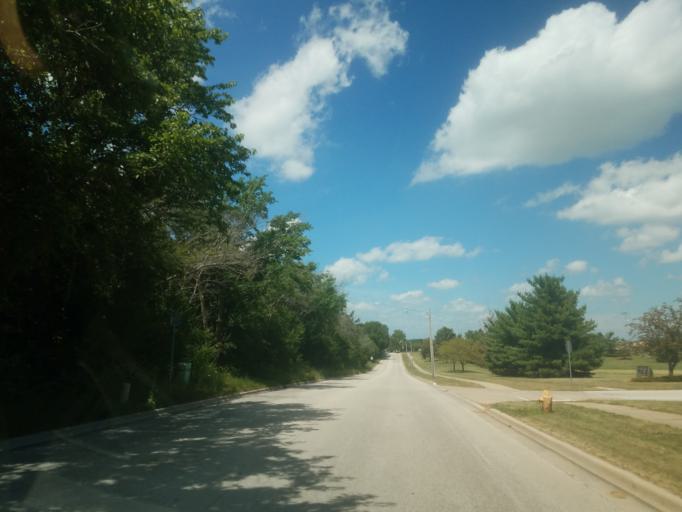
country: US
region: Illinois
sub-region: McLean County
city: Bloomington
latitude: 40.4479
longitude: -89.0296
